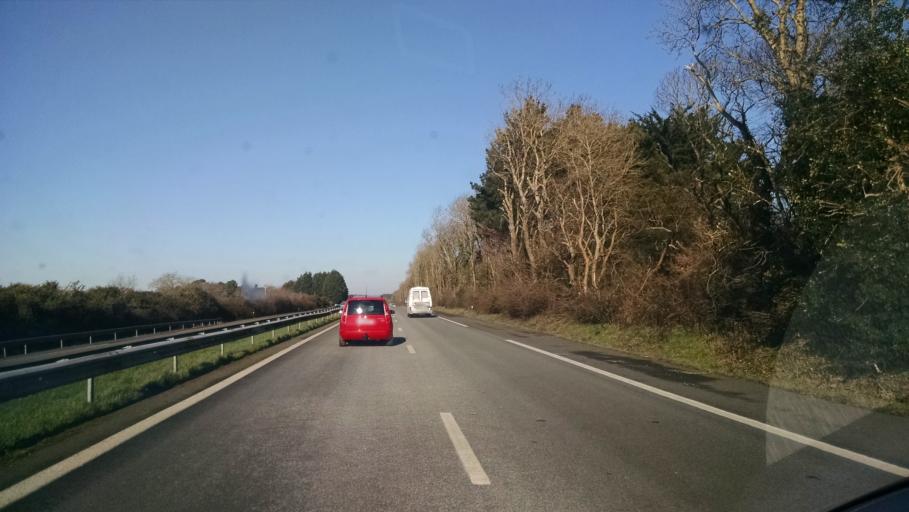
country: FR
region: Brittany
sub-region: Departement du Morbihan
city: Landaul
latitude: 47.7098
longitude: -3.0517
